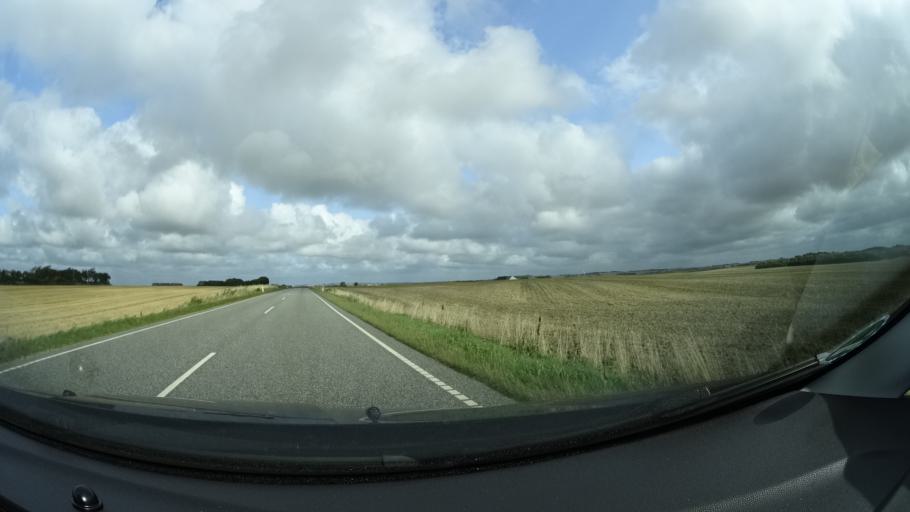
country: DK
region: Central Jutland
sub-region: Lemvig Kommune
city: Harboore
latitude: 56.5536
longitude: 8.1939
